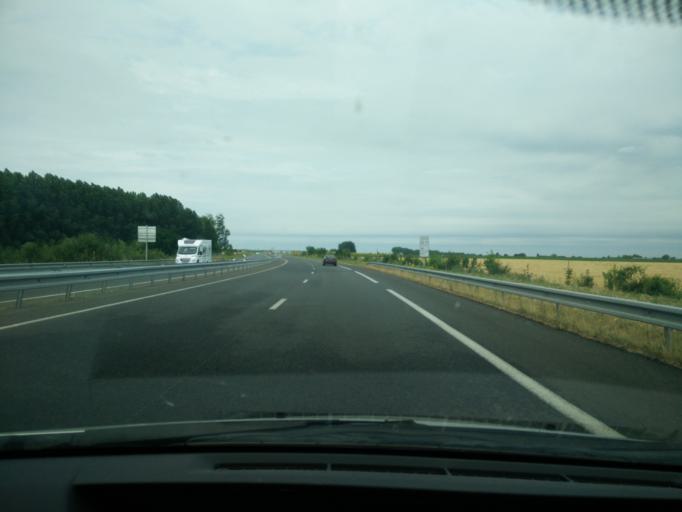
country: FR
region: Pays de la Loire
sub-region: Departement de Maine-et-Loire
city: Saint-Jean
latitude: 47.2860
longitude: -0.3592
